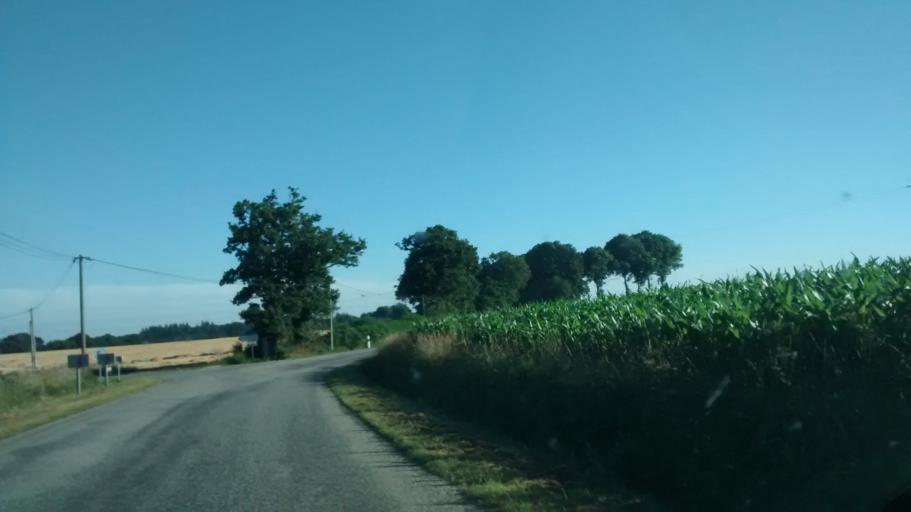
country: FR
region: Brittany
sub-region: Departement du Morbihan
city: Campeneac
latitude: 47.9714
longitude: -2.3058
